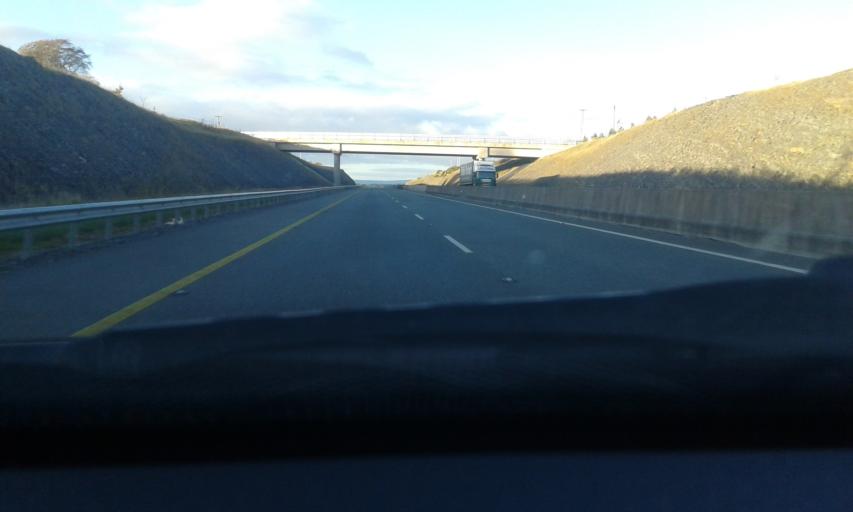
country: IE
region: Leinster
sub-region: Laois
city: Rathdowney
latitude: 52.8225
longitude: -7.4960
